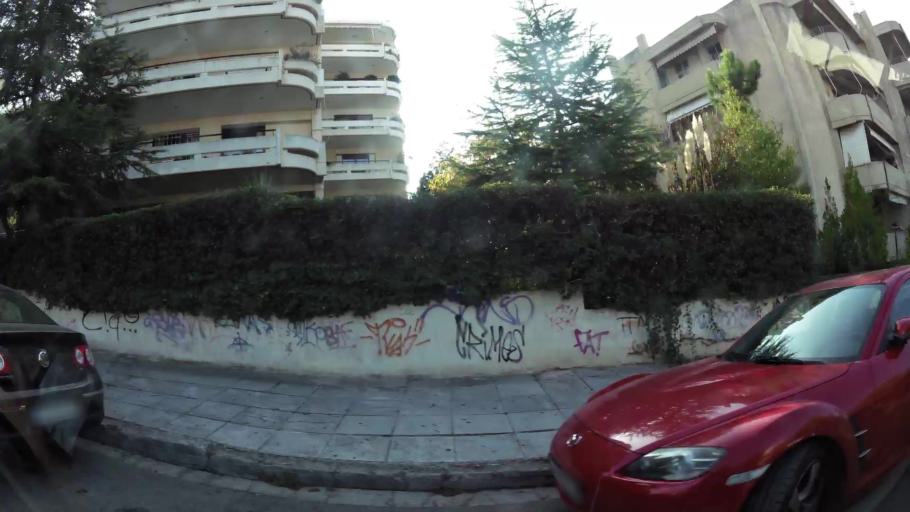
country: GR
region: Attica
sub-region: Nomarchia Athinas
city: Agia Paraskevi
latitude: 38.0067
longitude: 23.8231
